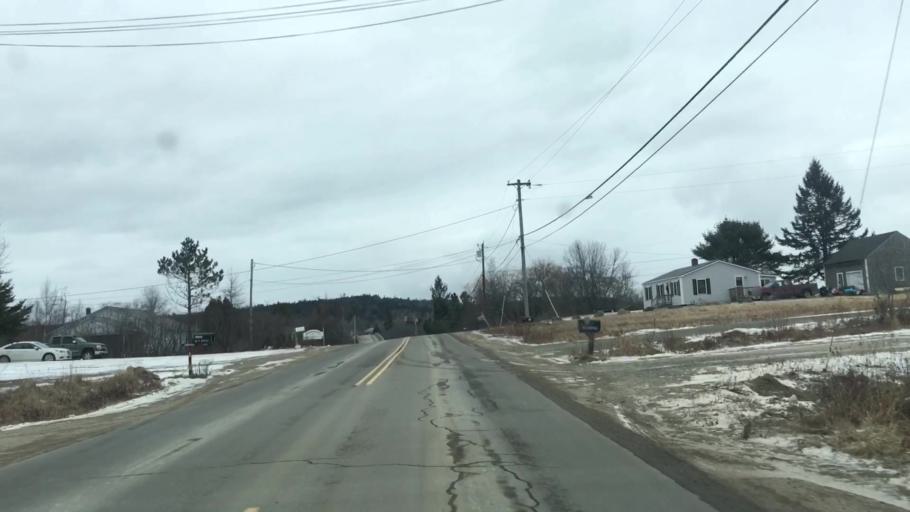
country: US
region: Maine
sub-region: Washington County
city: Machiasport
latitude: 44.7116
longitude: -67.4030
